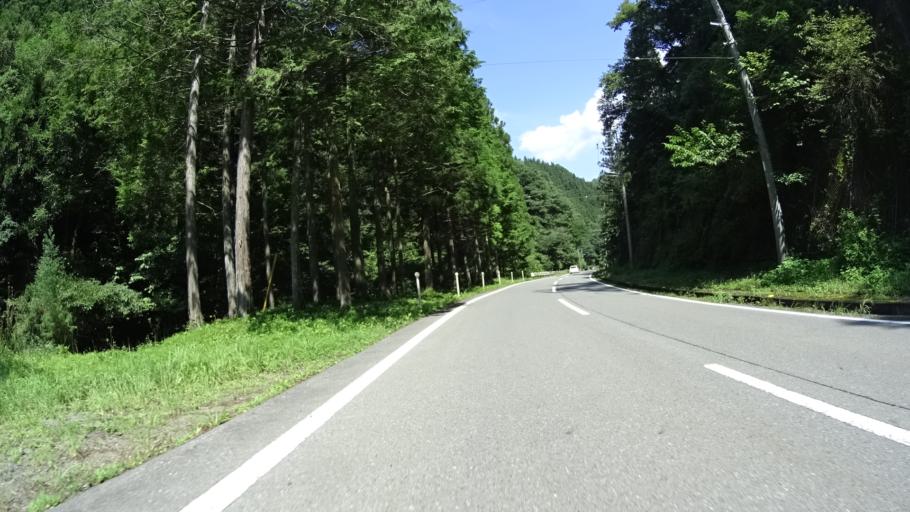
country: JP
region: Gunma
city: Tomioka
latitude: 36.0753
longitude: 138.8263
